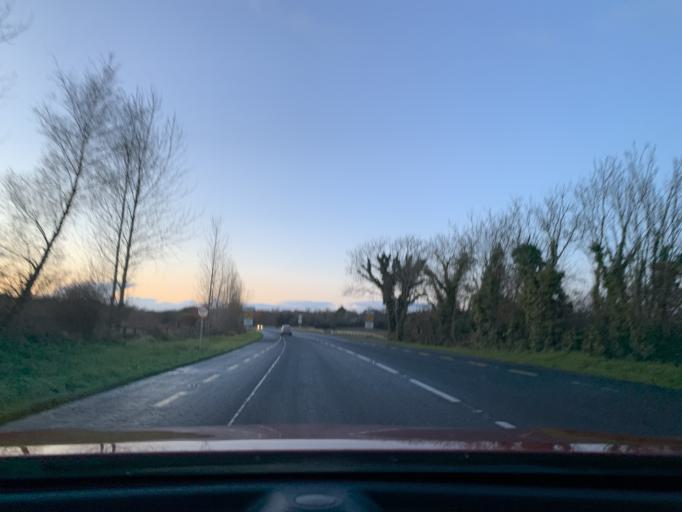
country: IE
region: Connaught
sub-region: County Leitrim
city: Carrick-on-Shannon
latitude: 53.9164
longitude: -7.9765
